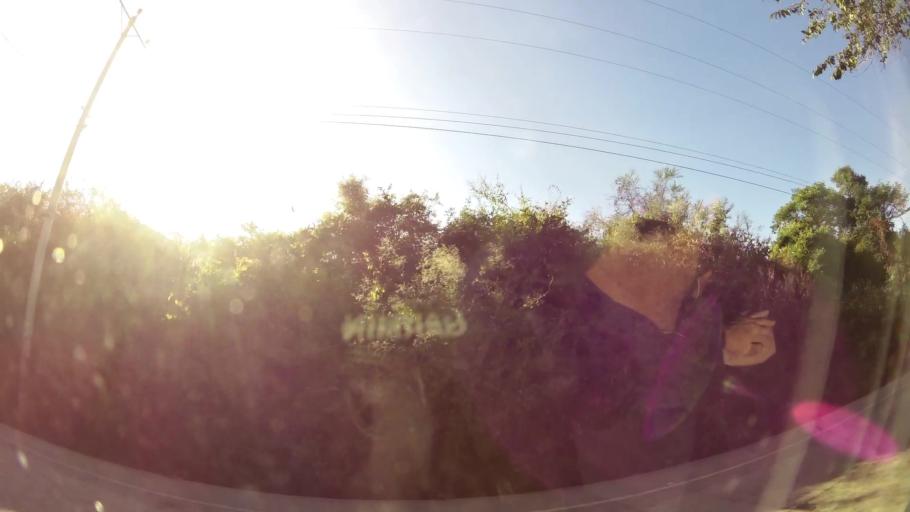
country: SV
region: Santa Ana
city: Texistepeque
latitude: 14.0735
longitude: -89.5027
